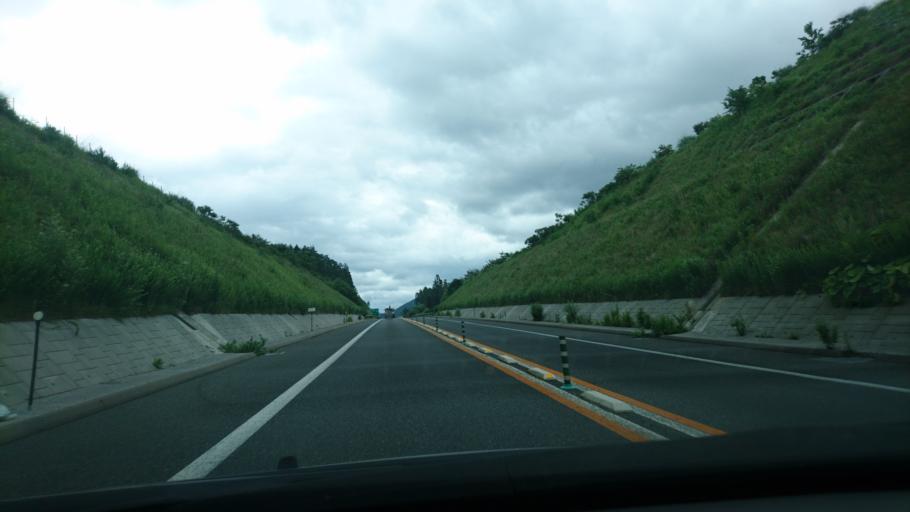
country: JP
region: Iwate
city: Ofunato
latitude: 39.0307
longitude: 141.6445
